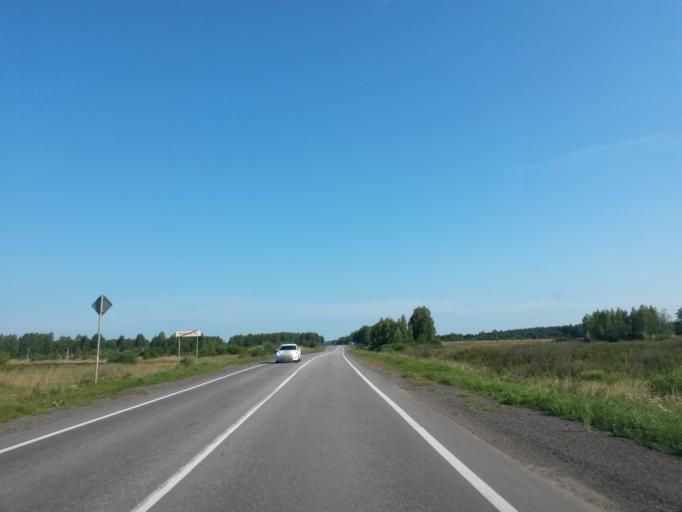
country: RU
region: Jaroslavl
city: Gavrilov-Yam
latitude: 57.3546
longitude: 39.9083
